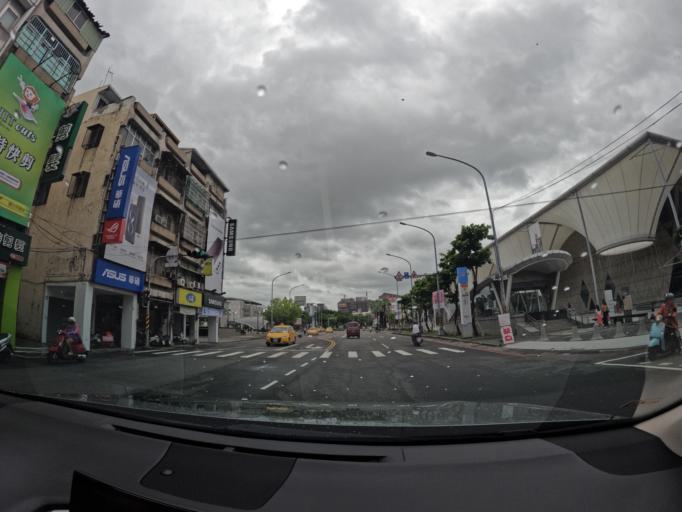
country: TW
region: Taiwan
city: Fengshan
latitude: 22.6253
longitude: 120.3626
